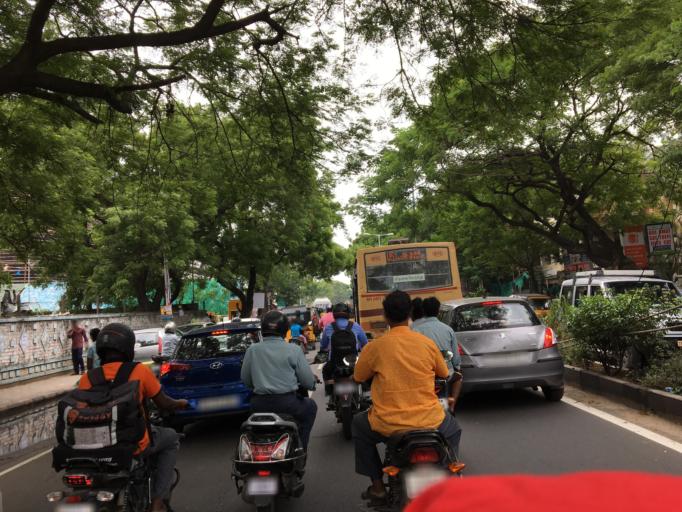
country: IN
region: Tamil Nadu
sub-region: Kancheepuram
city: Alandur
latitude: 12.9925
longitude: 80.2188
